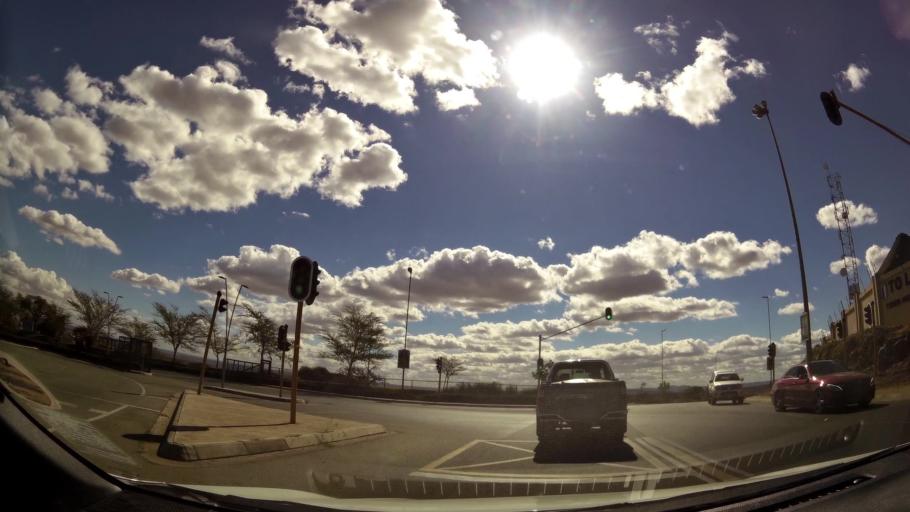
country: ZA
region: Limpopo
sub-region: Capricorn District Municipality
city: Polokwane
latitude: -23.8705
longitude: 29.5094
